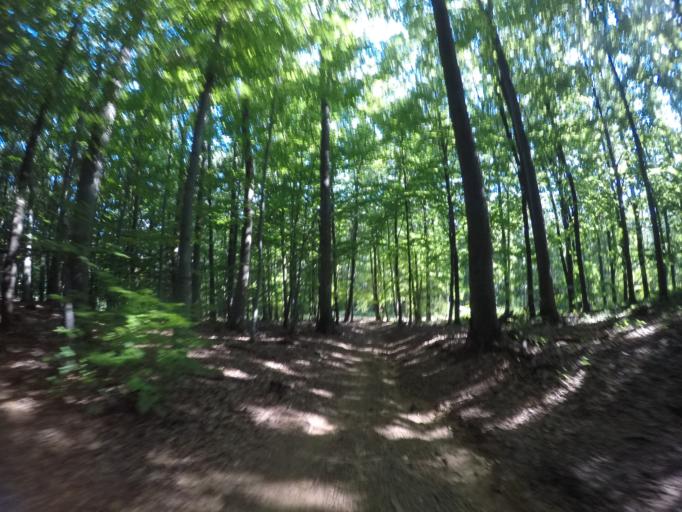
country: SK
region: Kosicky
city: Kosice
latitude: 48.7437
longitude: 21.1877
